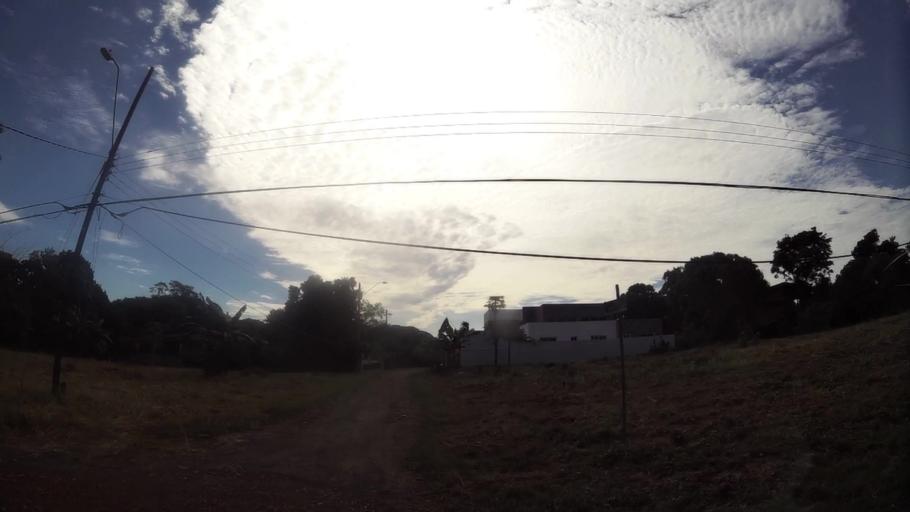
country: PA
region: Panama
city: Nueva Gorgona
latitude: 8.5319
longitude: -79.8801
